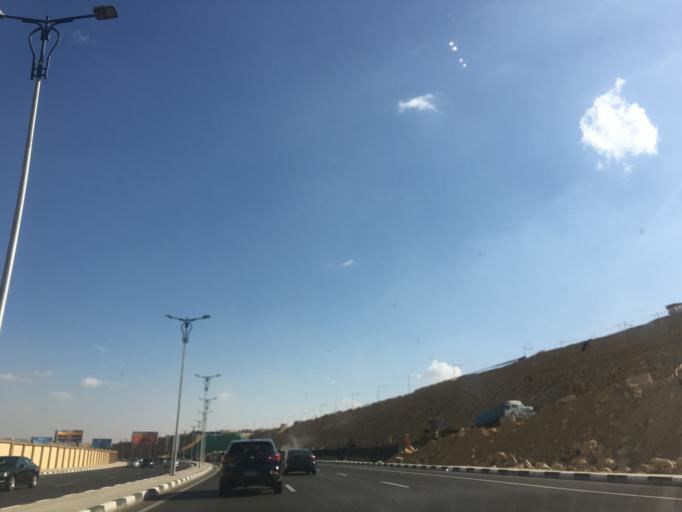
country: EG
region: Muhafazat al Qahirah
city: Cairo
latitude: 30.0292
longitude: 31.3108
